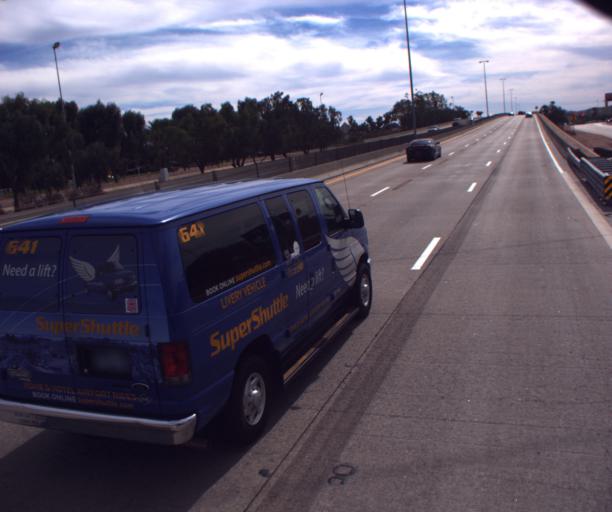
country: US
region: Arizona
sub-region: Maricopa County
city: Tempe Junction
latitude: 33.4258
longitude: -111.9781
